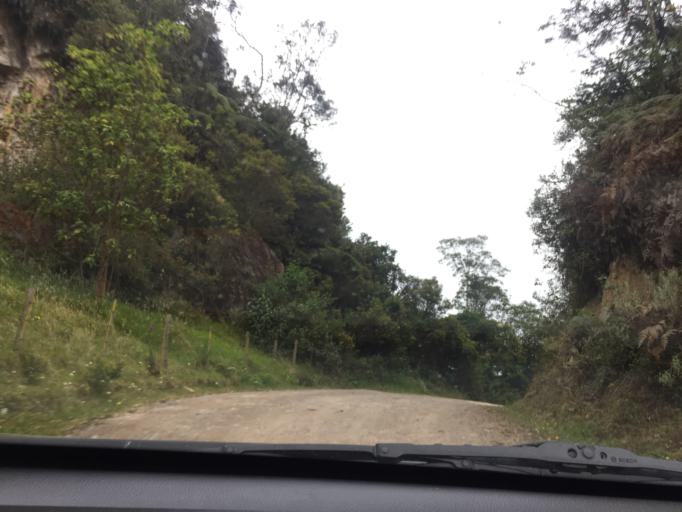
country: CO
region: Cundinamarca
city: Bojaca
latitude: 4.7079
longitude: -74.3555
